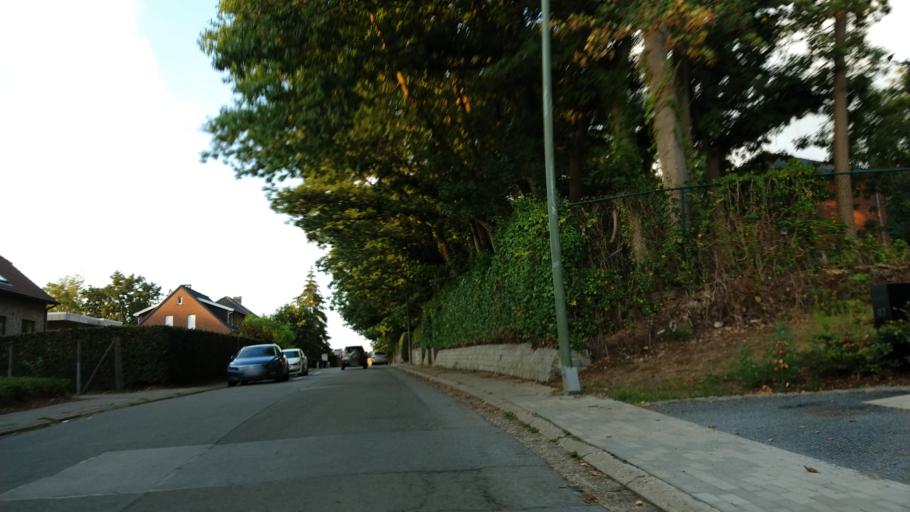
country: BE
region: Flanders
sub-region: Provincie Vlaams-Brabant
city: Oud-Heverlee
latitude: 50.8524
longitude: 4.6731
